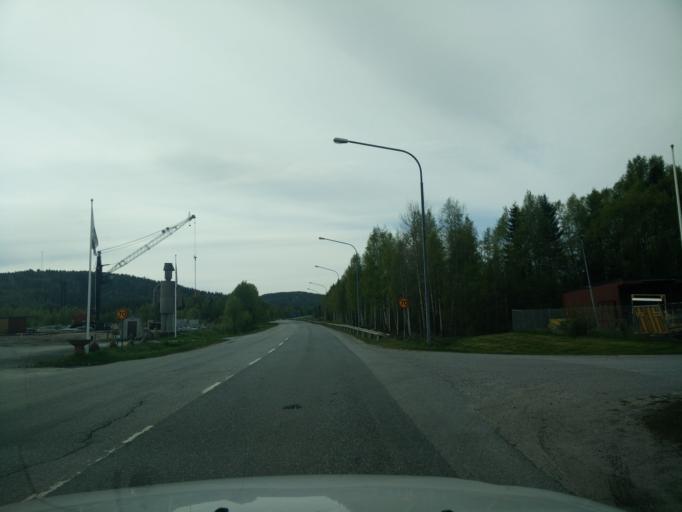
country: SE
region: Vaesternorrland
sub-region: OErnskoeldsviks Kommun
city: Bjasta
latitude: 63.1994
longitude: 18.4973
